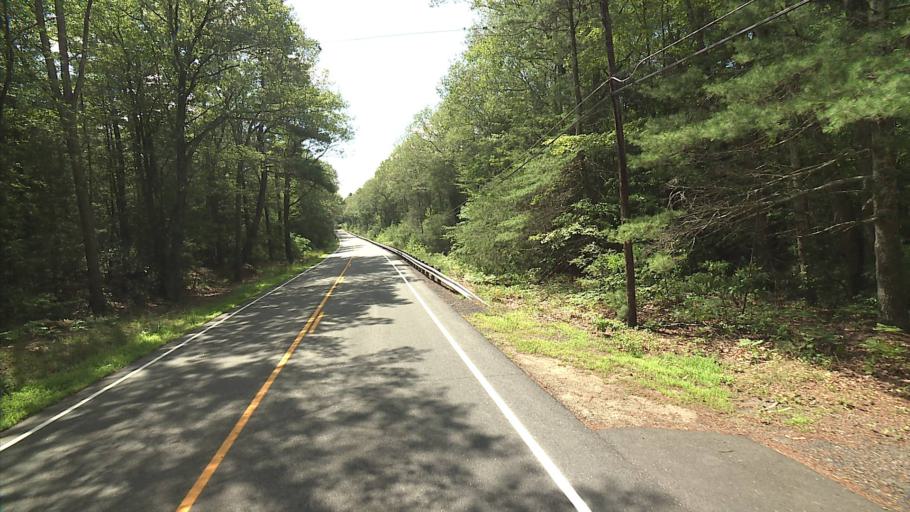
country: US
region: Massachusetts
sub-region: Worcester County
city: Southbridge
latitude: 42.0035
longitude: -72.0829
